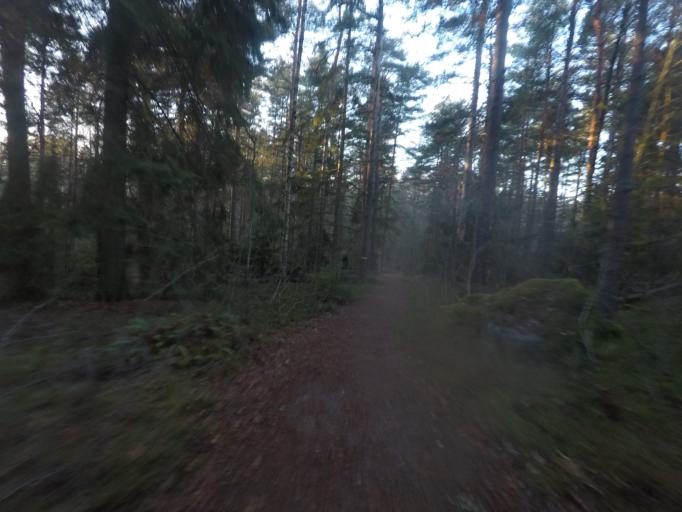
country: SE
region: Soedermanland
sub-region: Eskilstuna Kommun
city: Eskilstuna
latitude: 59.3898
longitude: 16.5277
